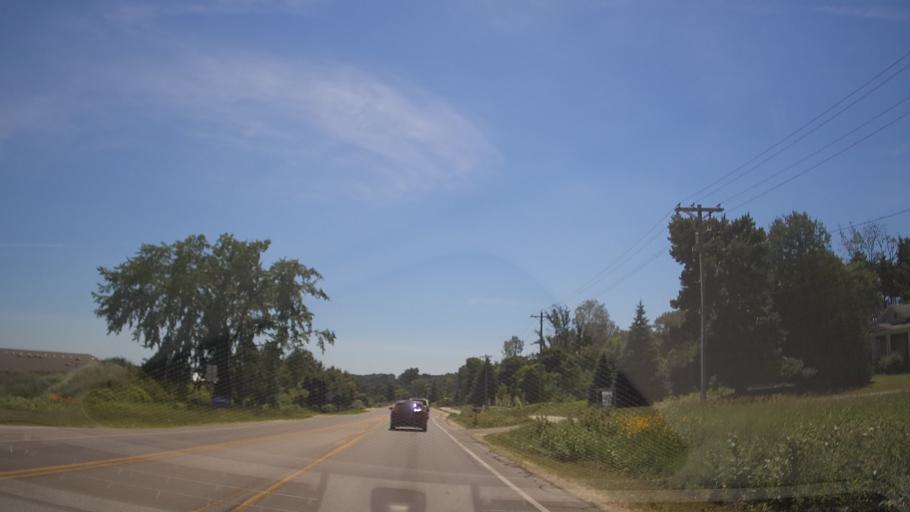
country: US
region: Michigan
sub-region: Grand Traverse County
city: Traverse City
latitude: 44.7400
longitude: -85.6558
